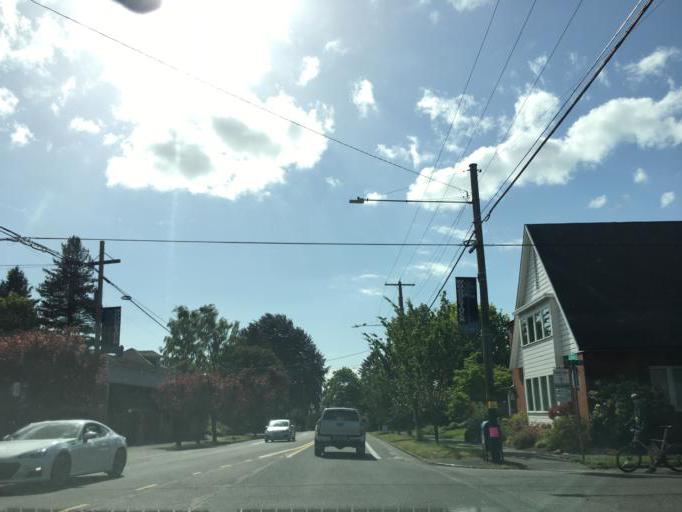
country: US
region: Oregon
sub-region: Clackamas County
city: Milwaukie
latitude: 45.4792
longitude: -122.6205
